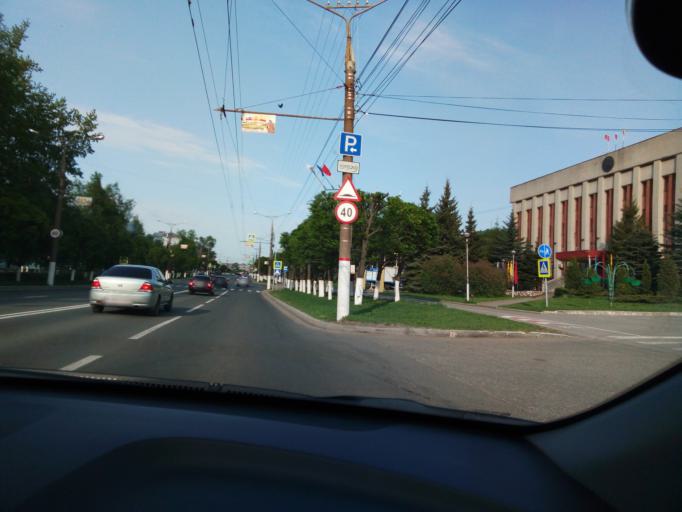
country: RU
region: Chuvashia
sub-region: Cheboksarskiy Rayon
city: Cheboksary
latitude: 56.1248
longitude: 47.2586
